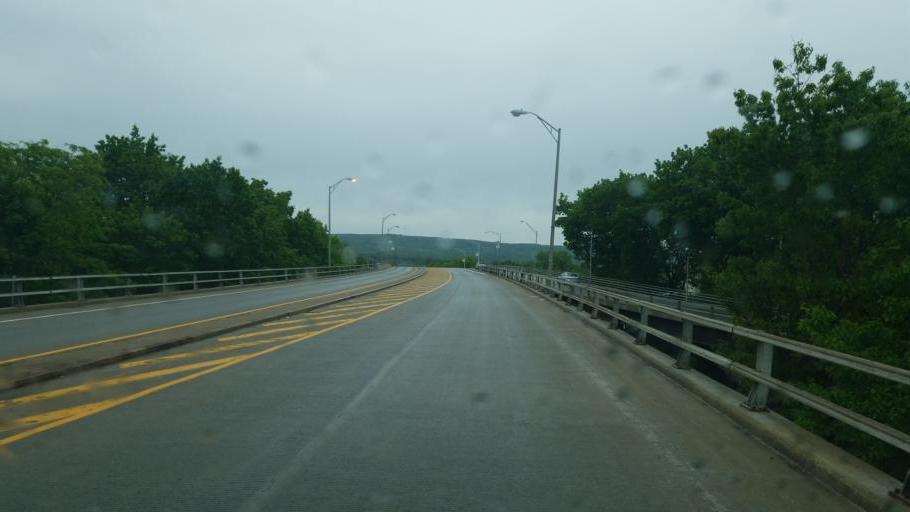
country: US
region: New York
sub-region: Oneida County
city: Utica
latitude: 43.1041
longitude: -75.2255
